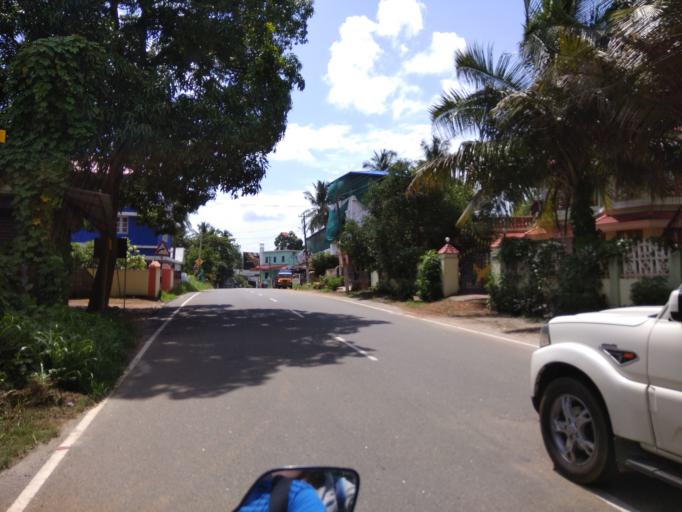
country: IN
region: Kerala
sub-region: Thrissur District
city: Trichur
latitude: 10.5454
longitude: 76.3244
